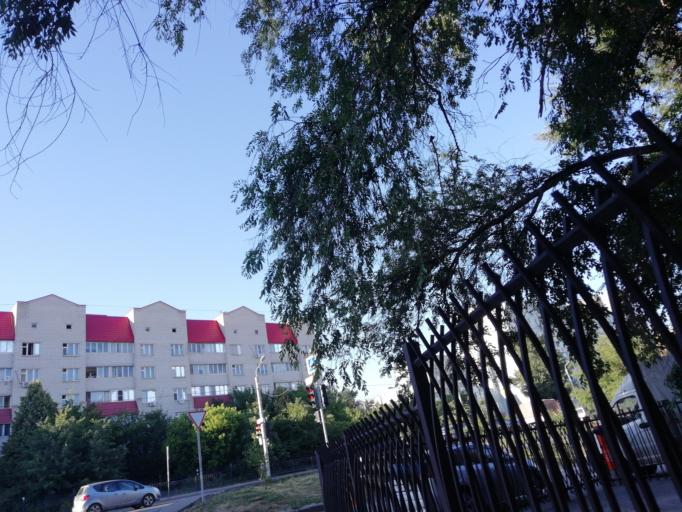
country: RU
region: Rostov
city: Severnyy
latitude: 47.2893
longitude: 39.7105
